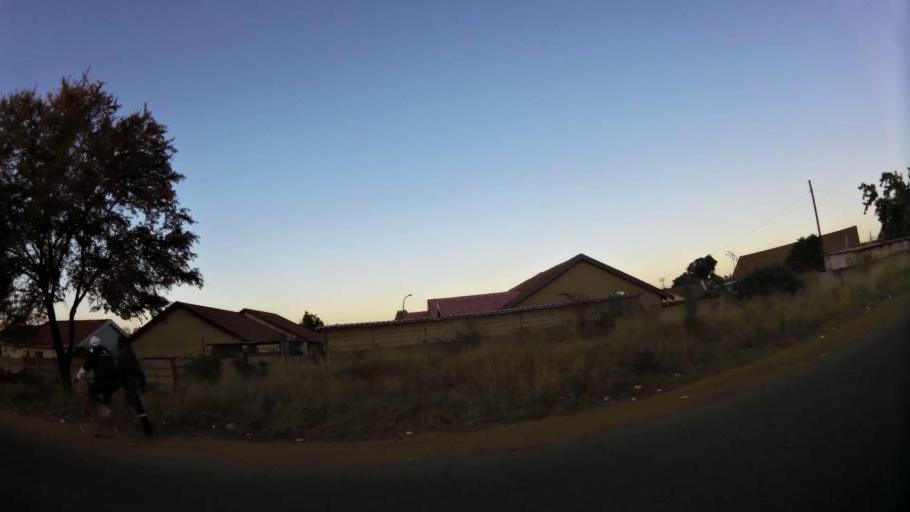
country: ZA
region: North-West
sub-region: Bojanala Platinum District Municipality
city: Rustenburg
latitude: -25.6384
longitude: 27.2004
